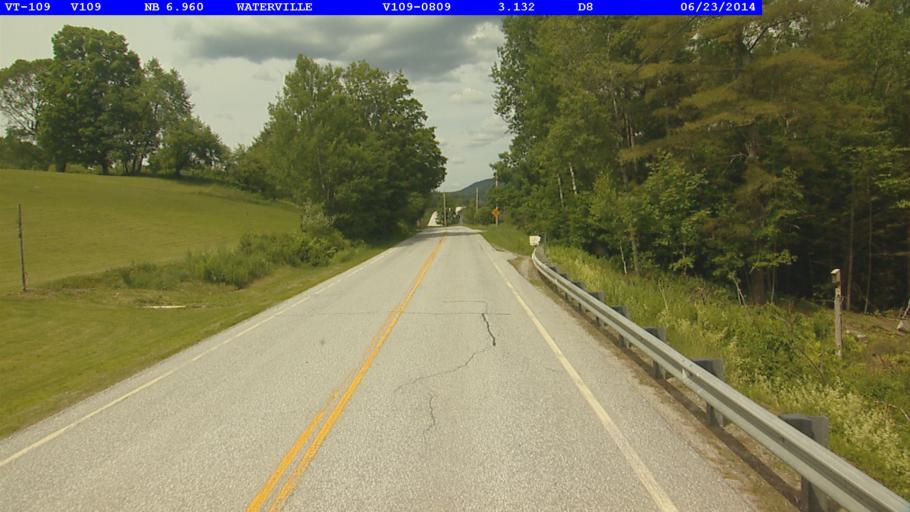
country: US
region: Vermont
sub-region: Lamoille County
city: Johnson
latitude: 44.7227
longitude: -72.7494
